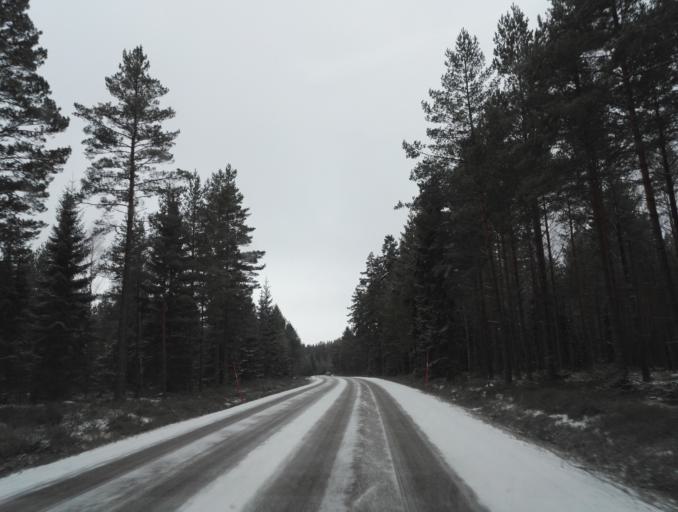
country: SE
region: Kronoberg
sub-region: Lessebo Kommun
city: Lessebo
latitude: 56.8164
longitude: 15.3758
